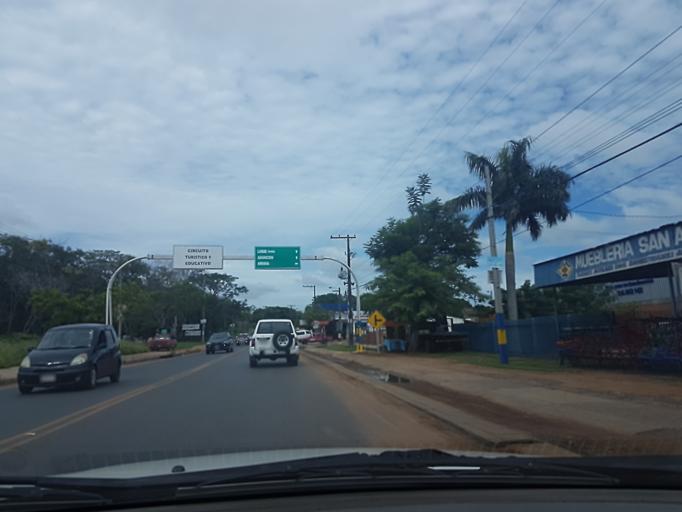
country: PY
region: Central
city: San Lorenzo
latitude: -25.2628
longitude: -57.4807
